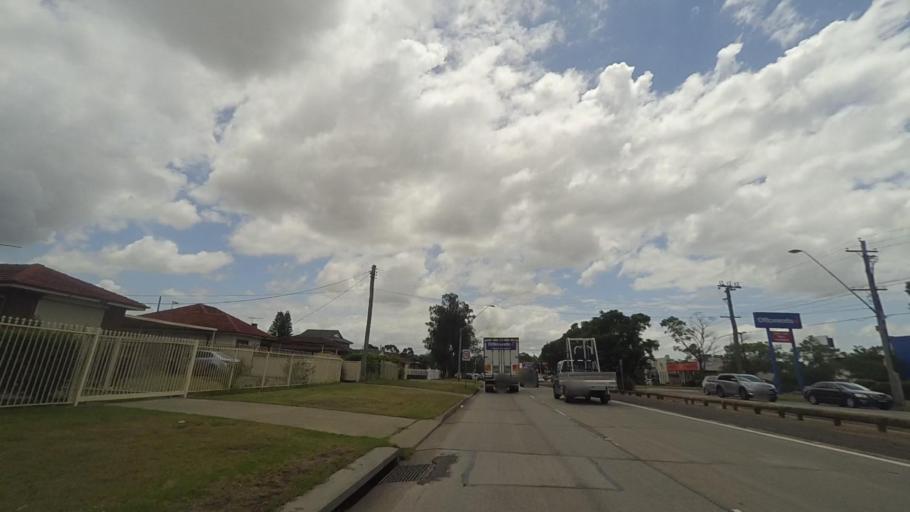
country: AU
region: New South Wales
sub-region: Fairfield
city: Cabramatta West
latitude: -33.9094
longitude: 150.9187
